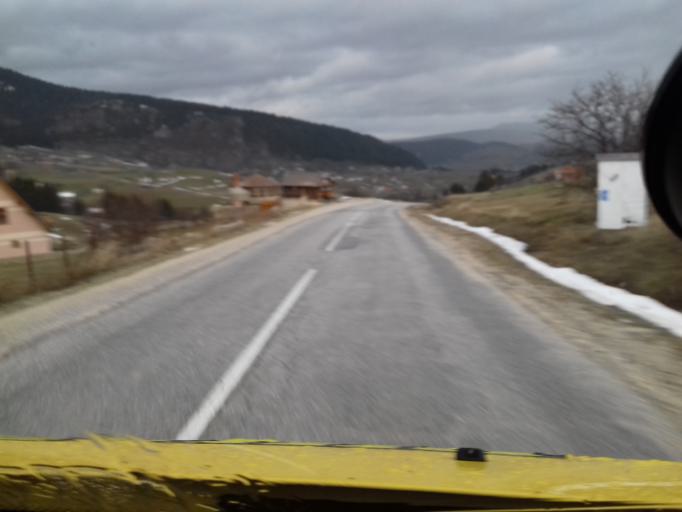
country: BA
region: Federation of Bosnia and Herzegovina
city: Turbe
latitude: 44.3093
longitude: 17.5433
